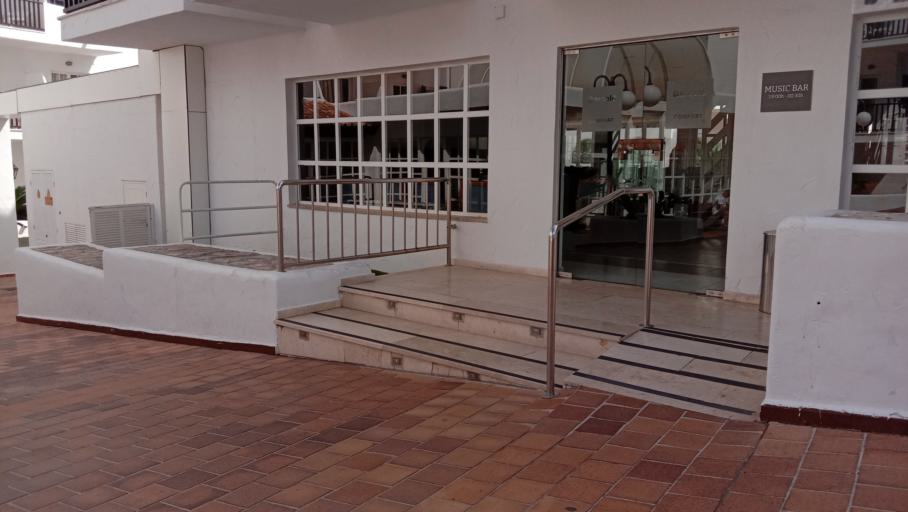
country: ES
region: Balearic Islands
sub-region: Illes Balears
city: Santanyi
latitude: 39.3791
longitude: 3.2385
